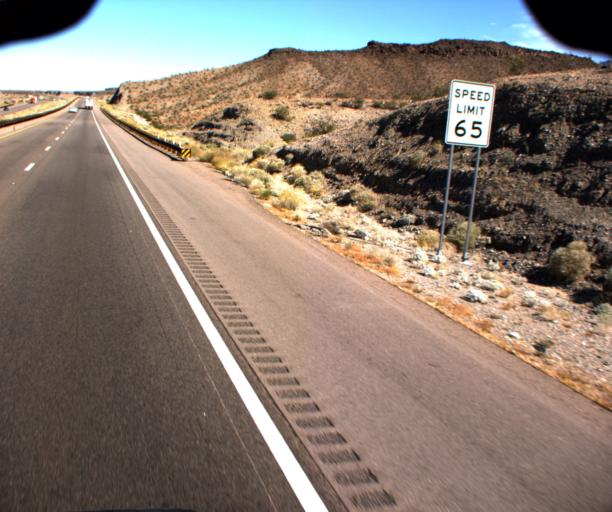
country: US
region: Nevada
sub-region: Clark County
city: Boulder City
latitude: 35.9372
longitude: -114.6389
